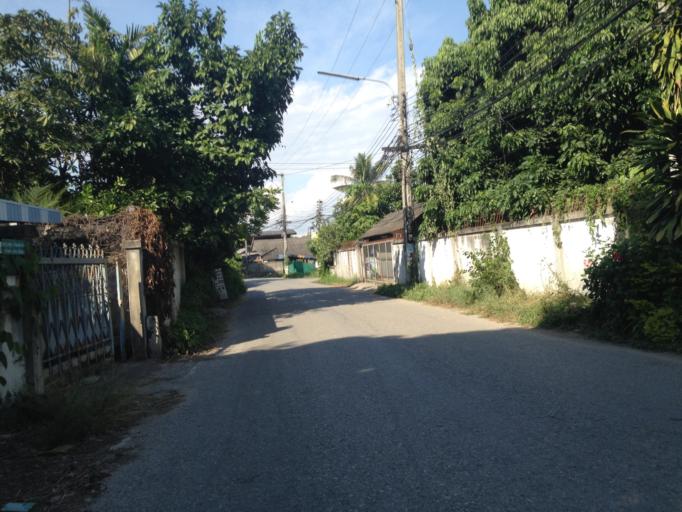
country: TH
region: Chiang Mai
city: Chiang Mai
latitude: 18.7590
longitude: 98.9824
